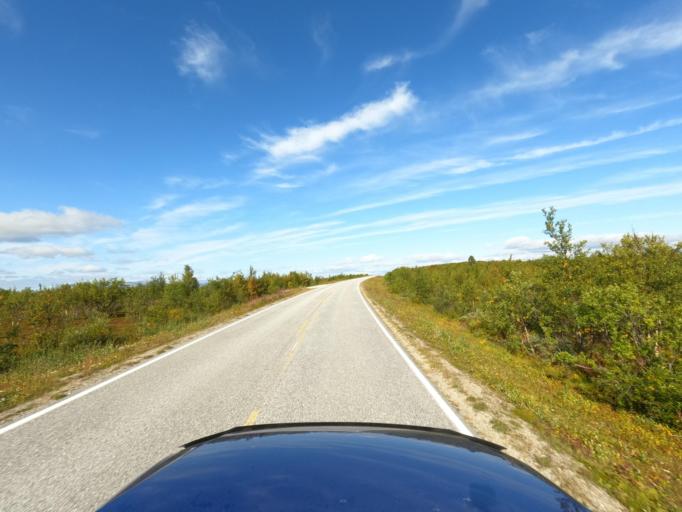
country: NO
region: Finnmark Fylke
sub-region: Karasjok
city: Karasjohka
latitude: 69.7109
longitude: 25.2419
